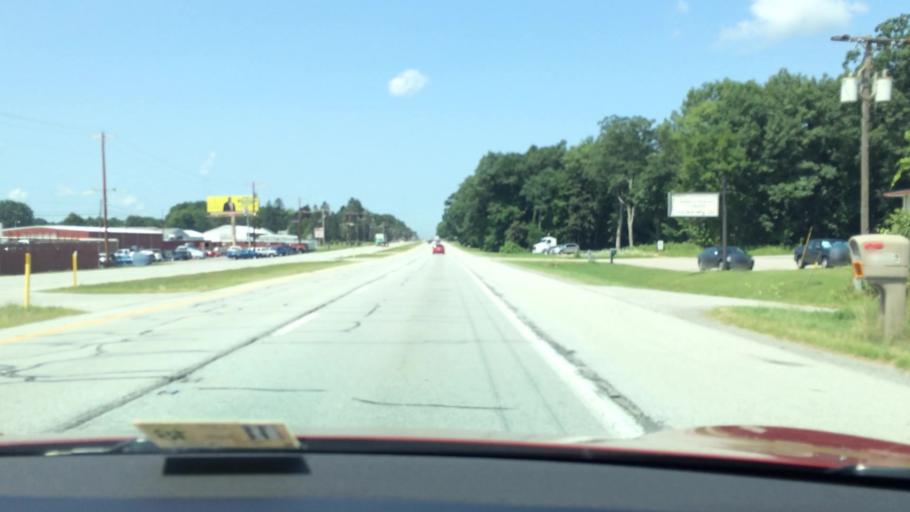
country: US
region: Indiana
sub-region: Saint Joseph County
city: South Bend
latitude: 41.6720
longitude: -86.3670
